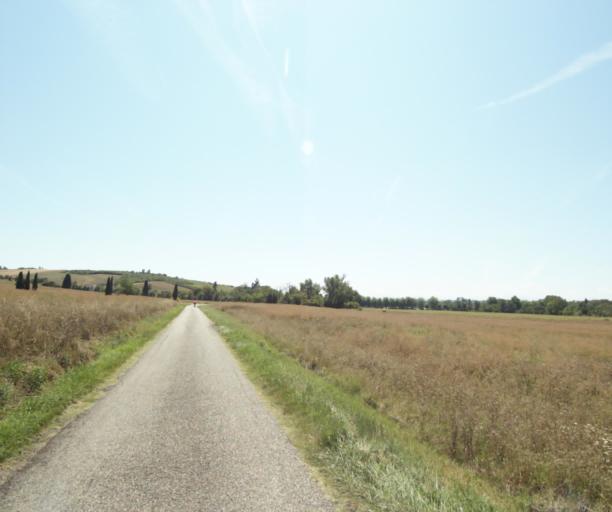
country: FR
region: Midi-Pyrenees
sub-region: Departement de l'Ariege
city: Lezat-sur-Leze
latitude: 43.2804
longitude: 1.3566
